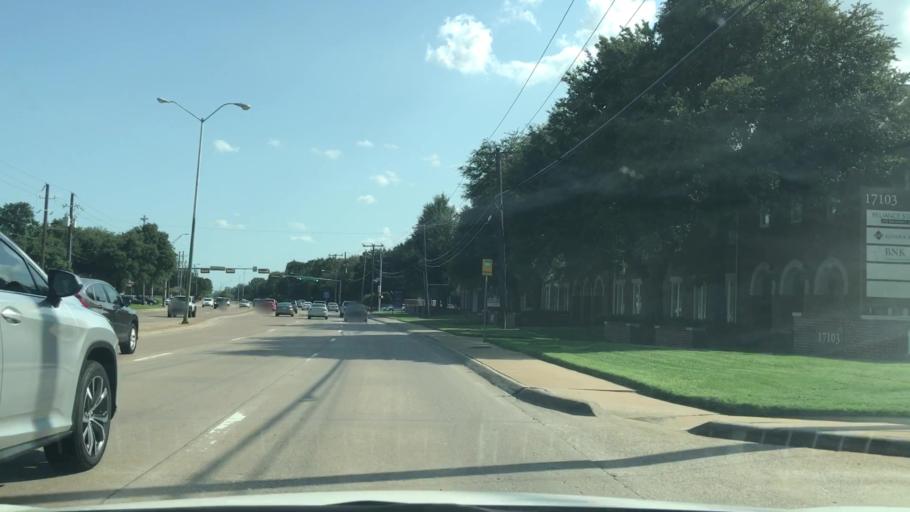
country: US
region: Texas
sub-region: Dallas County
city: Addison
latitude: 32.9848
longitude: -96.8042
